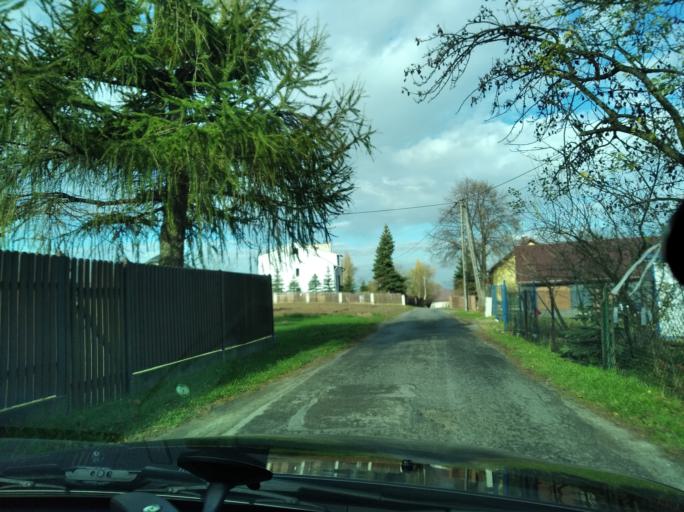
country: PL
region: Subcarpathian Voivodeship
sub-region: Powiat debicki
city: Debica
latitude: 50.0344
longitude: 21.4525
